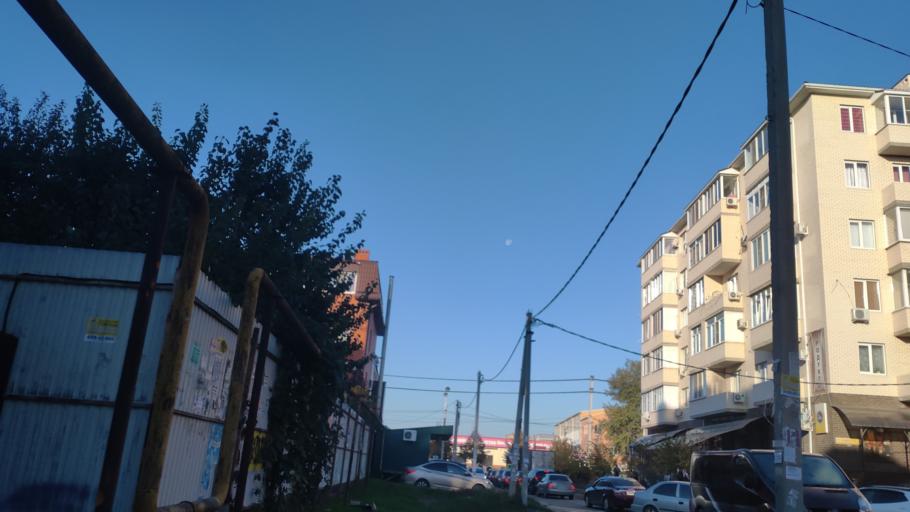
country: RU
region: Krasnodarskiy
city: Krasnodar
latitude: 45.0829
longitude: 39.0029
